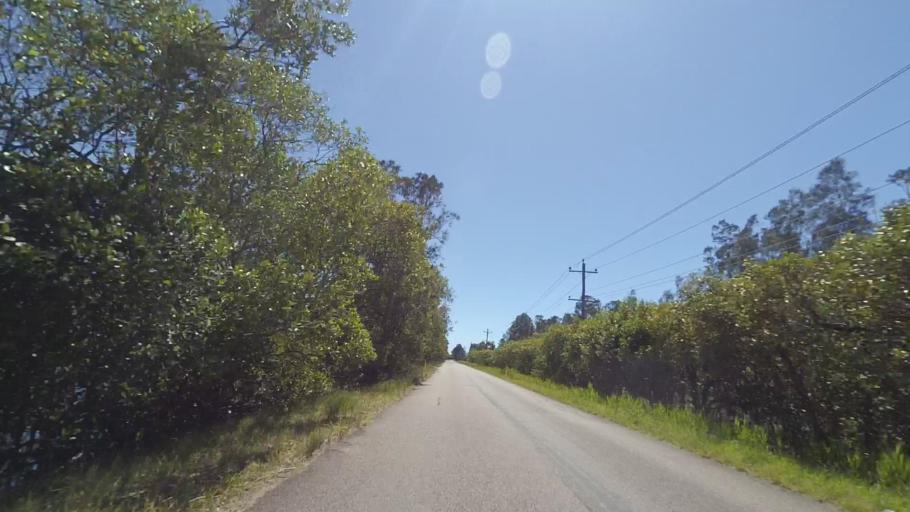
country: AU
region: New South Wales
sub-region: Port Stephens Shire
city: Medowie
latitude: -32.7851
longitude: 151.9384
